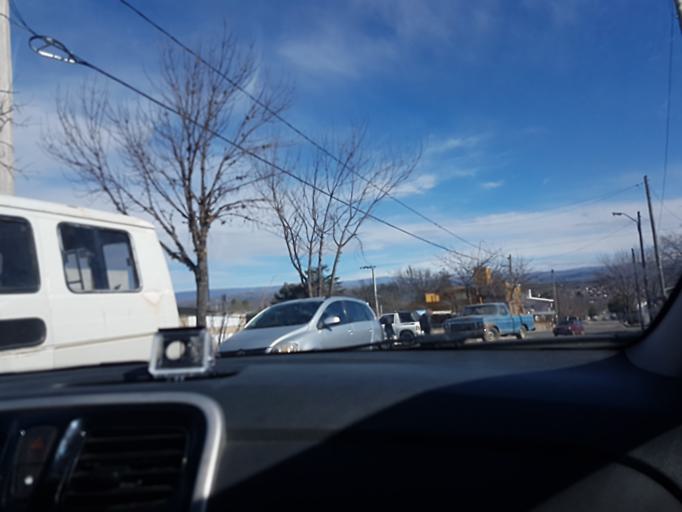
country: AR
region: Cordoba
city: Villa Carlos Paz
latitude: -31.4363
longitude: -64.5005
